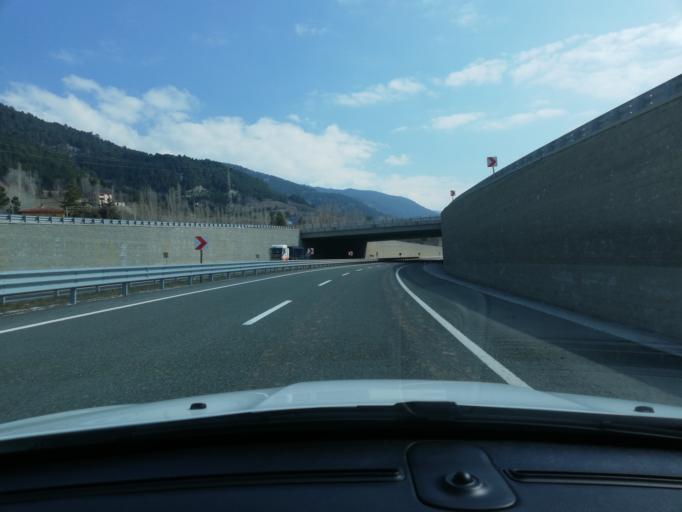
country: TR
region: Cankiri
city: Ilgaz
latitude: 41.0258
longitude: 33.7185
